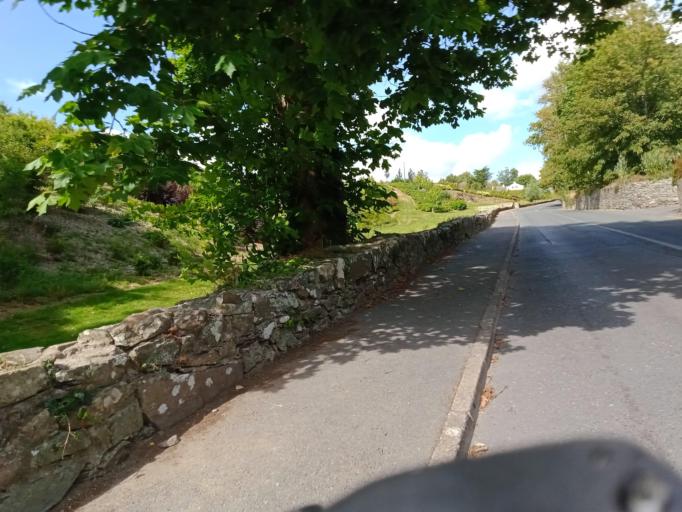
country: IE
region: Munster
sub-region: Waterford
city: Dungarvan
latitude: 52.1279
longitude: -7.4603
